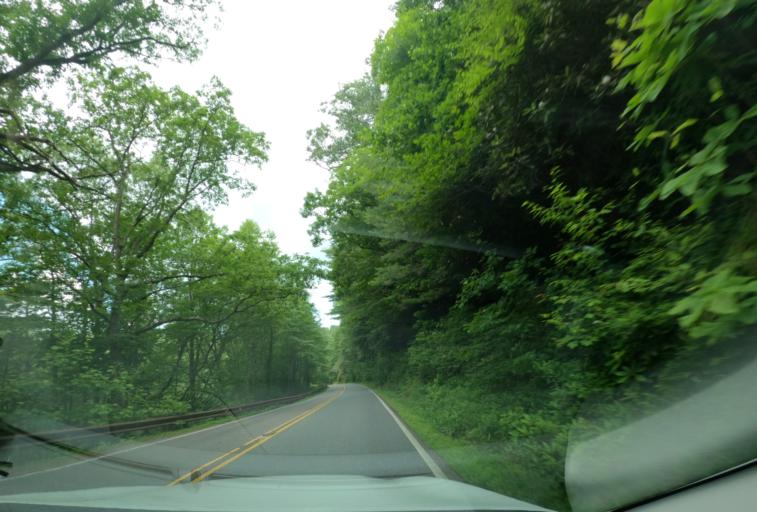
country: US
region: North Carolina
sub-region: Macon County
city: Franklin
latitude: 35.0697
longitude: -83.2287
